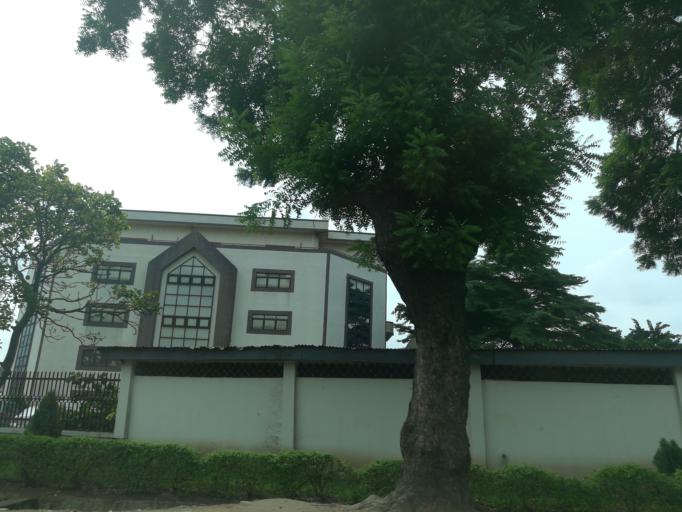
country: NG
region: Lagos
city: Ojota
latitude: 6.6004
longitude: 3.3764
